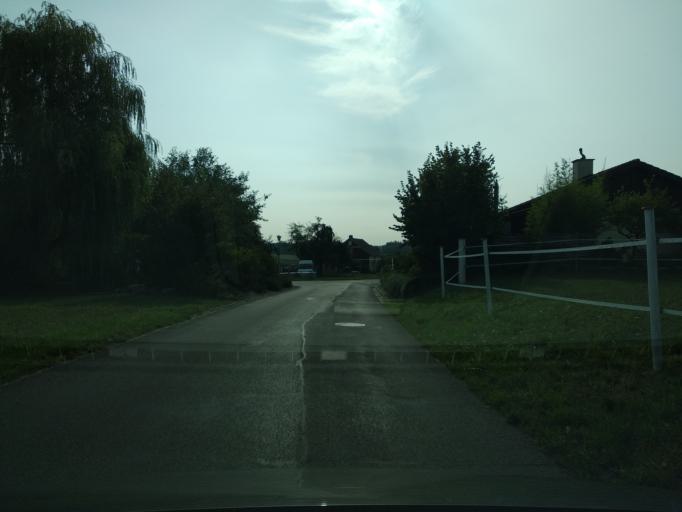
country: DE
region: Baden-Wuerttemberg
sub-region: Freiburg Region
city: Busingen
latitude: 47.6586
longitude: 8.6962
